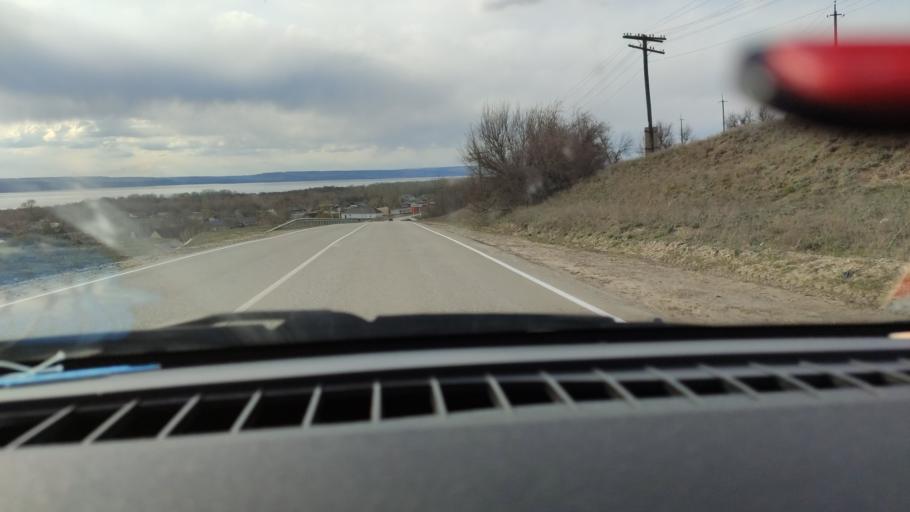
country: RU
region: Saratov
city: Privolzhskiy
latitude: 51.1825
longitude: 45.9190
